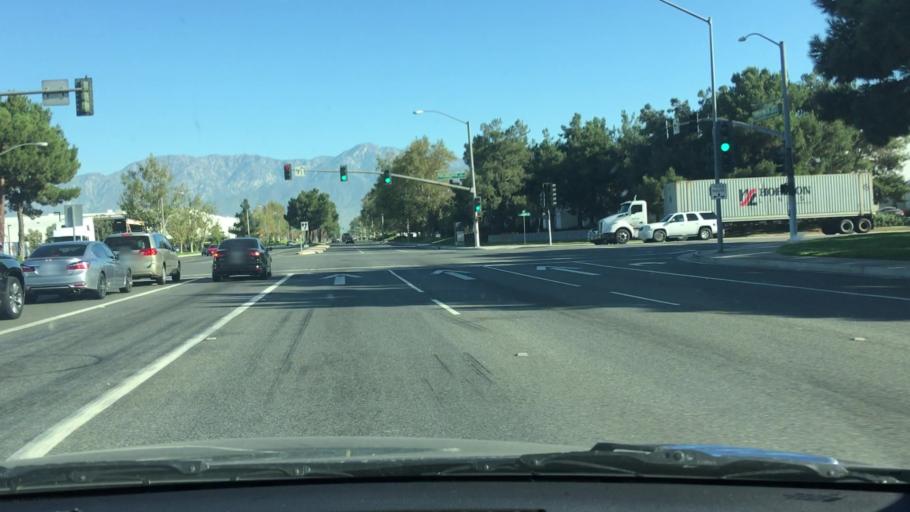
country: US
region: California
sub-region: San Bernardino County
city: Ontario
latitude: 34.0333
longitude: -117.5932
